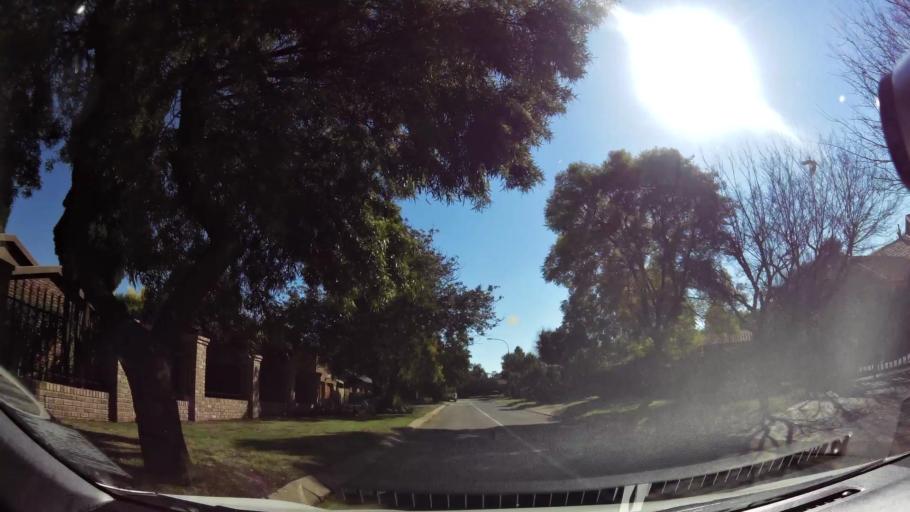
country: ZA
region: Gauteng
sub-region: Ekurhuleni Metropolitan Municipality
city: Germiston
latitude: -26.3008
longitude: 28.0962
